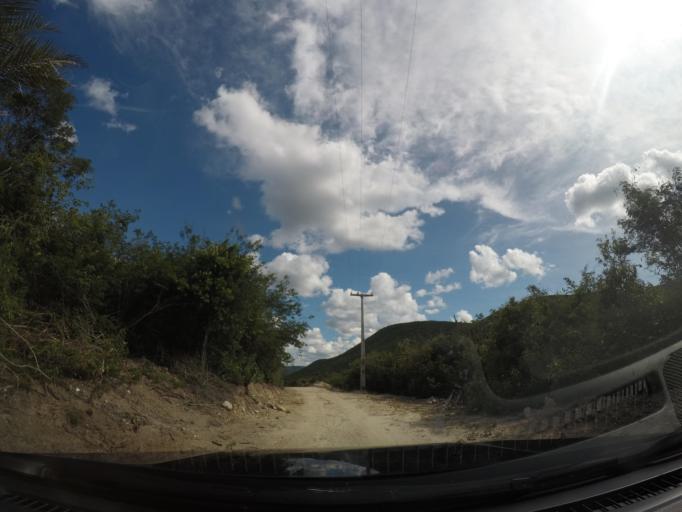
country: BR
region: Bahia
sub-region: Barra Da Estiva
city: Barra da Estiva
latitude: -13.1470
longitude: -41.5985
